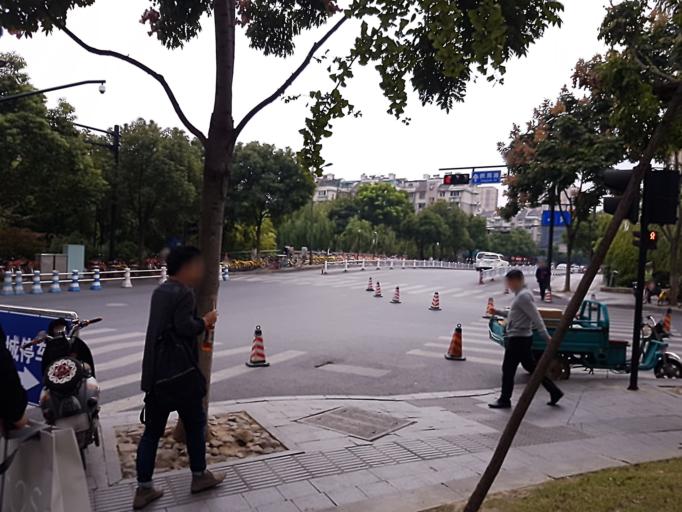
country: CN
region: Zhejiang Sheng
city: Gudang
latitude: 30.3013
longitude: 120.1045
